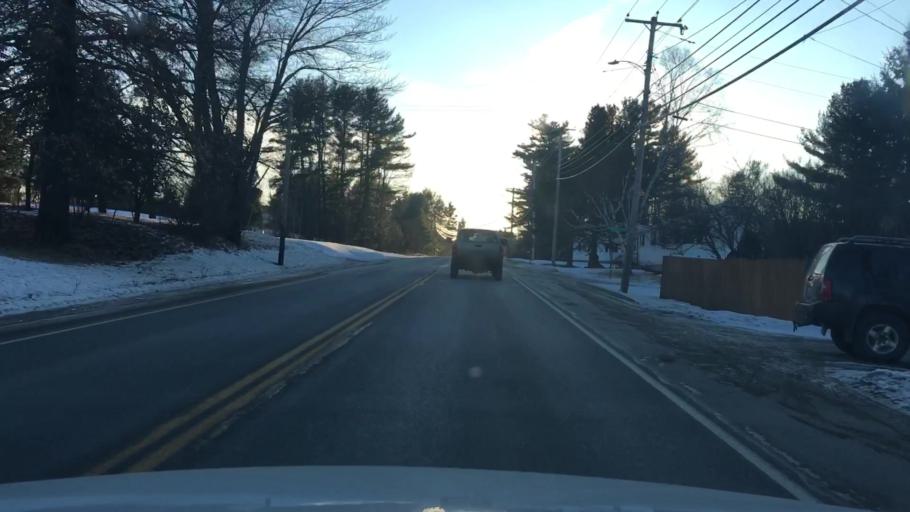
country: US
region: Maine
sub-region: Penobscot County
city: Brewer
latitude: 44.8074
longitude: -68.7399
